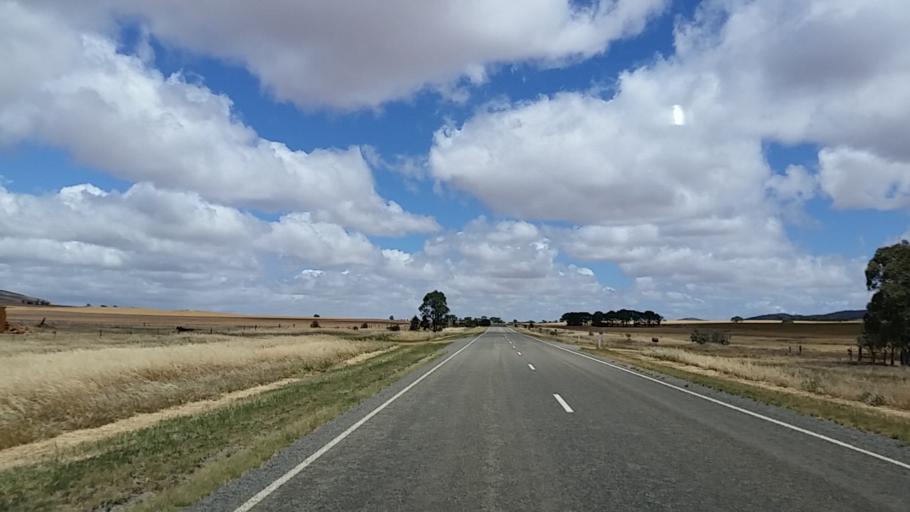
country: AU
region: South Australia
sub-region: Peterborough
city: Peterborough
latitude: -32.8613
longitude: 138.5419
